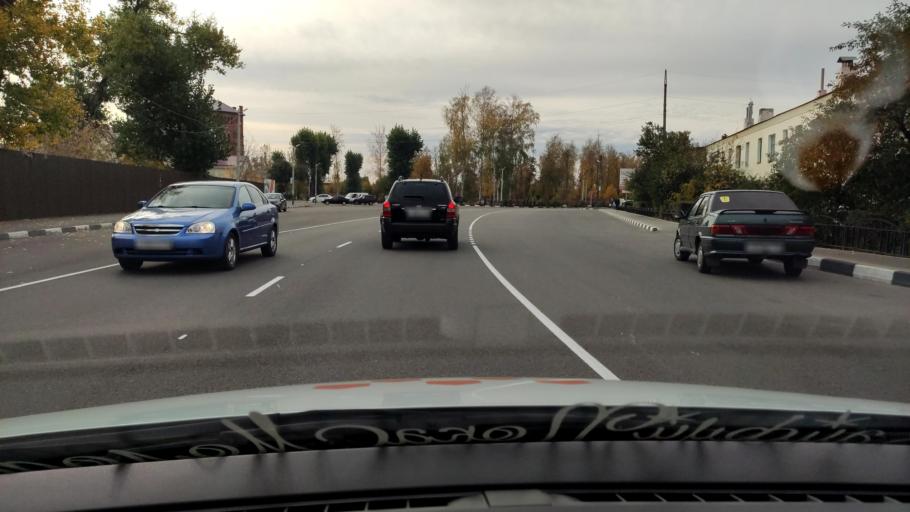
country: RU
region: Voronezj
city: Ramon'
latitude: 51.9117
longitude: 39.3385
